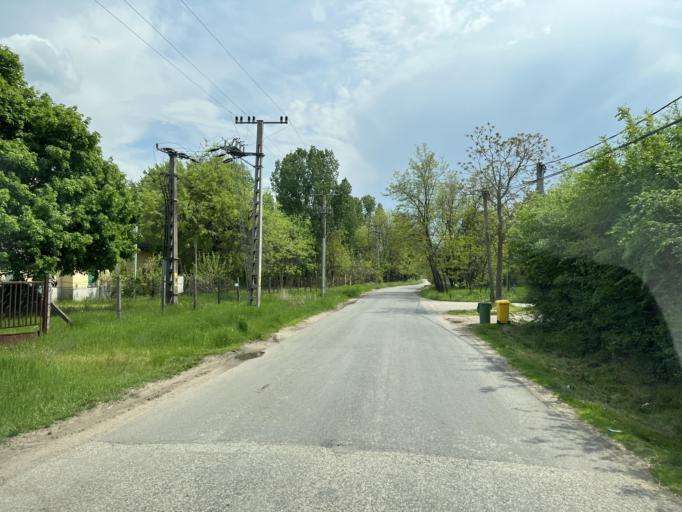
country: HU
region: Pest
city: Nagykoros
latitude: 47.0215
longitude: 19.7905
